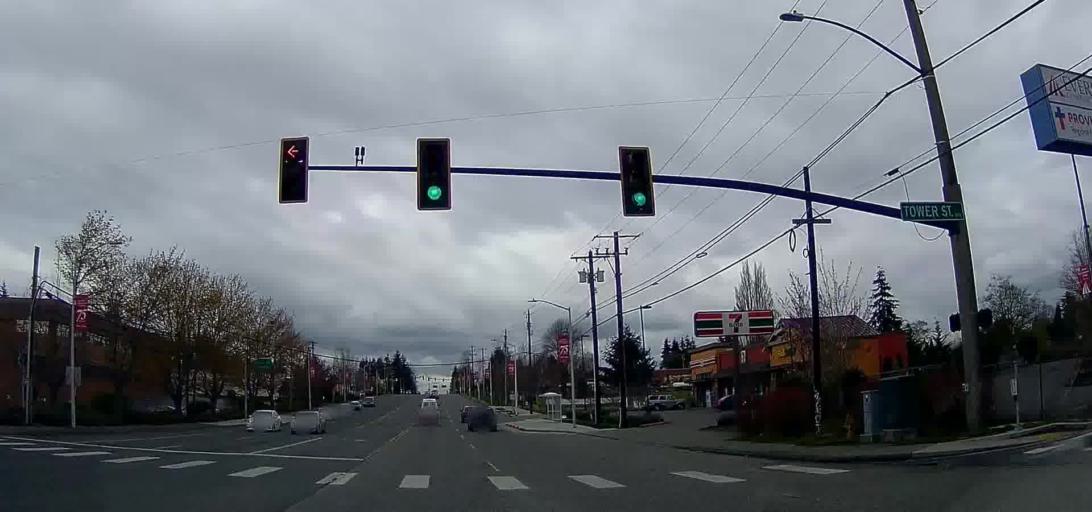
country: US
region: Washington
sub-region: Snohomish County
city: Everett
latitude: 48.0058
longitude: -122.1975
